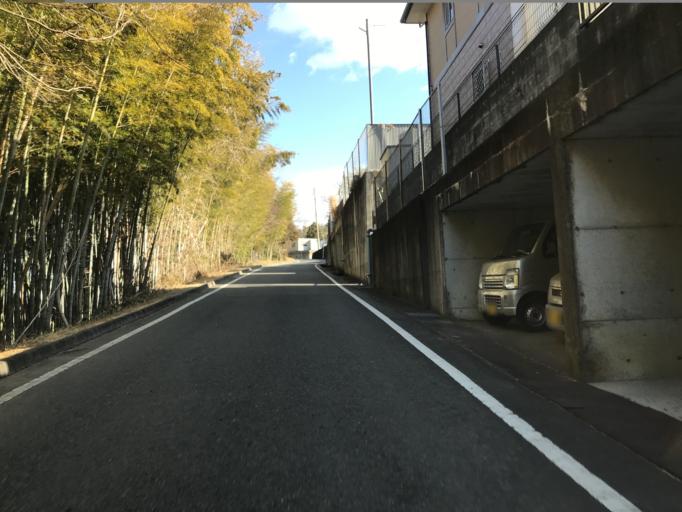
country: JP
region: Fukushima
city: Iwaki
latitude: 37.1254
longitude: 140.8427
